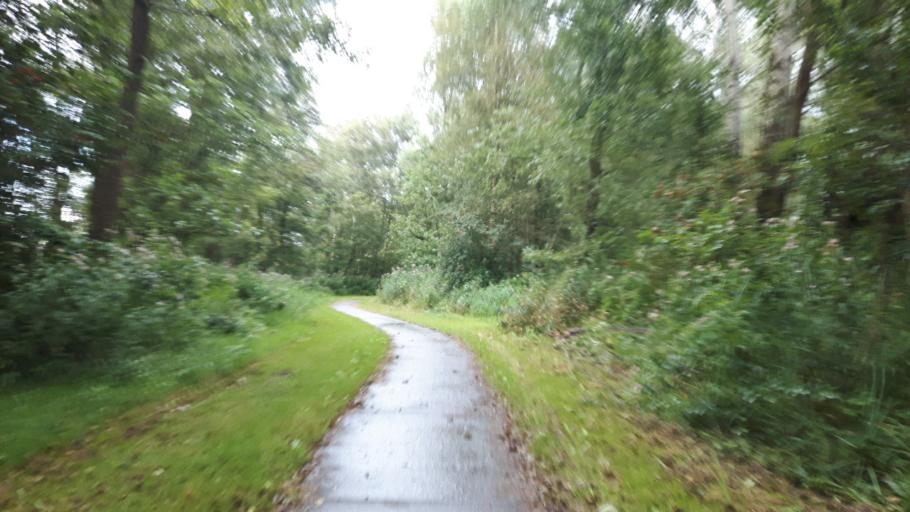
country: NL
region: Overijssel
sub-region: Gemeente Steenwijkerland
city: Blokzijl
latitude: 52.7646
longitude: 5.9596
